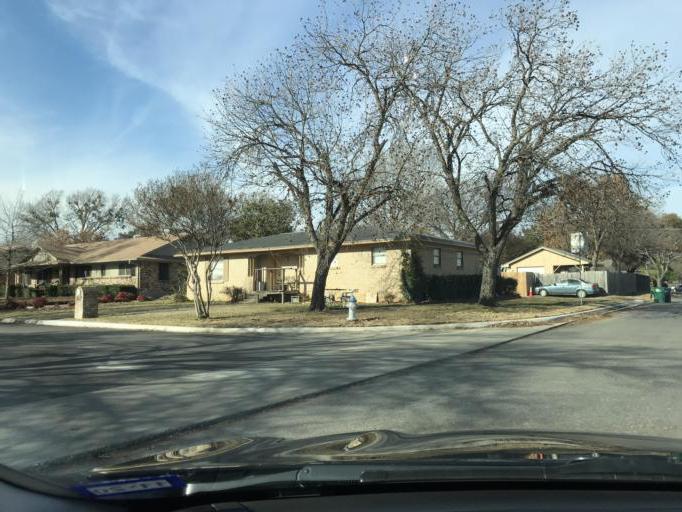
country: US
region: Texas
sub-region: Denton County
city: Denton
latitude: 33.2312
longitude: -97.1446
